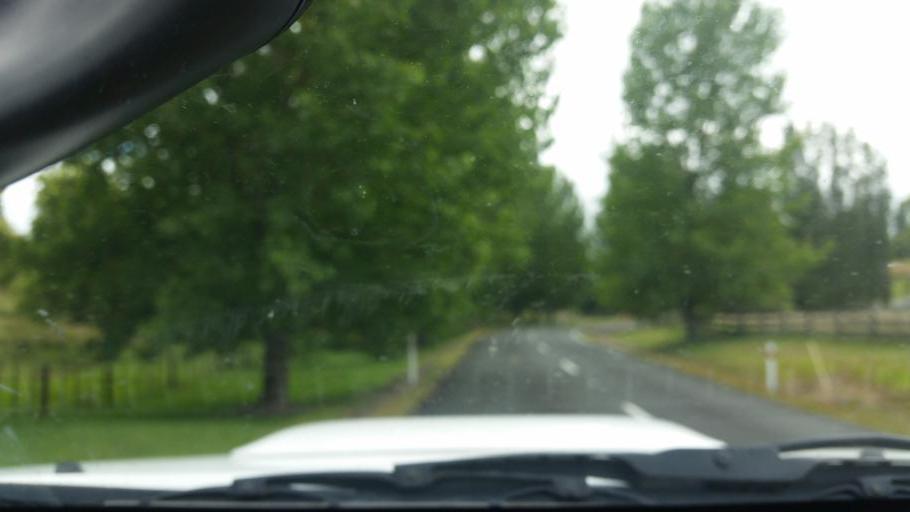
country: NZ
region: Auckland
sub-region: Auckland
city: Wellsford
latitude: -36.1315
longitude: 174.3600
